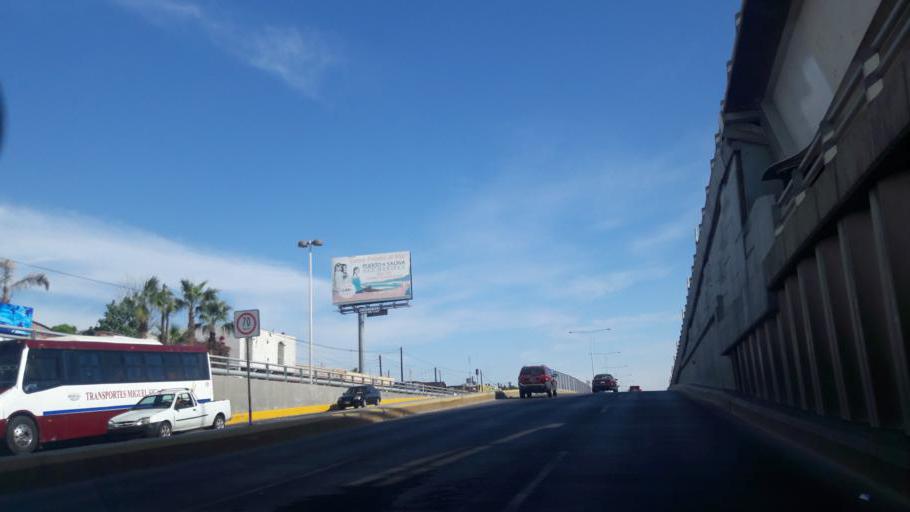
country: MX
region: Baja California
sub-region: Mexicali
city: Mexicali
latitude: 32.6245
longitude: -115.4508
